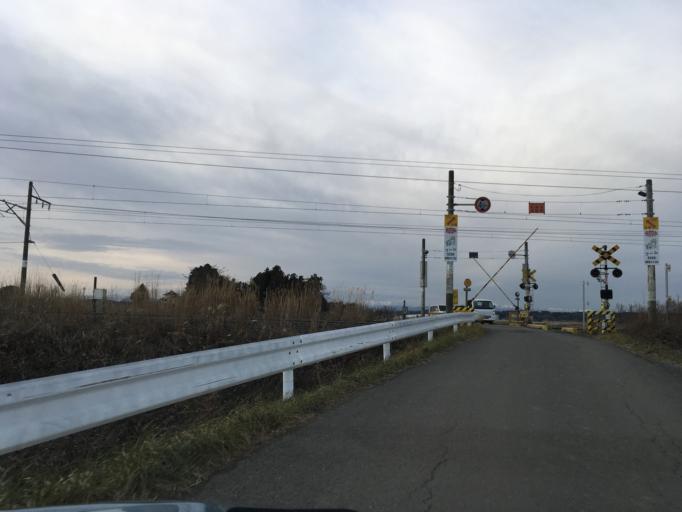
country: JP
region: Miyagi
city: Kogota
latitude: 38.6387
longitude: 141.0687
